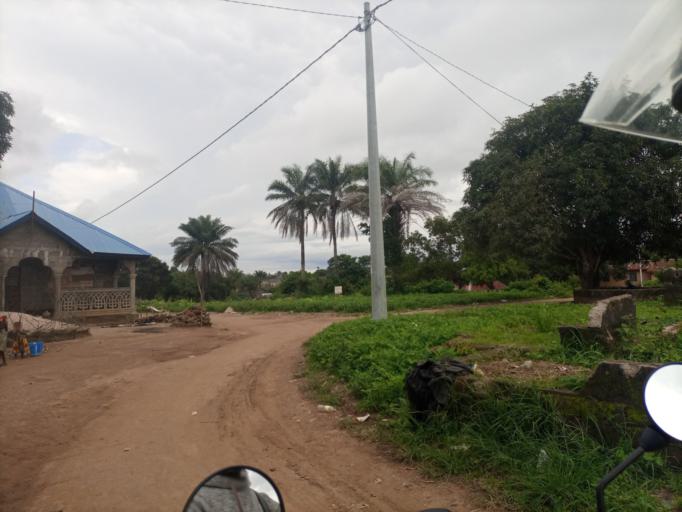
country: SL
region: Northern Province
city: Masoyila
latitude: 8.6046
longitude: -13.1729
